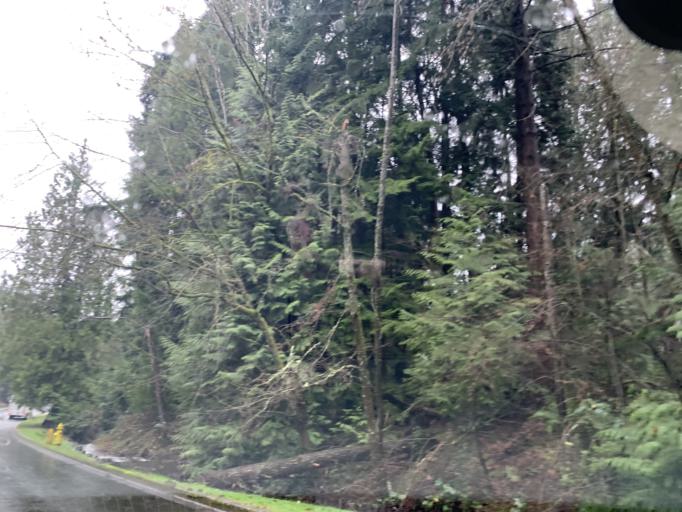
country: US
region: Washington
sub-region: King County
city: Kingsgate
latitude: 47.7351
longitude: -122.1797
